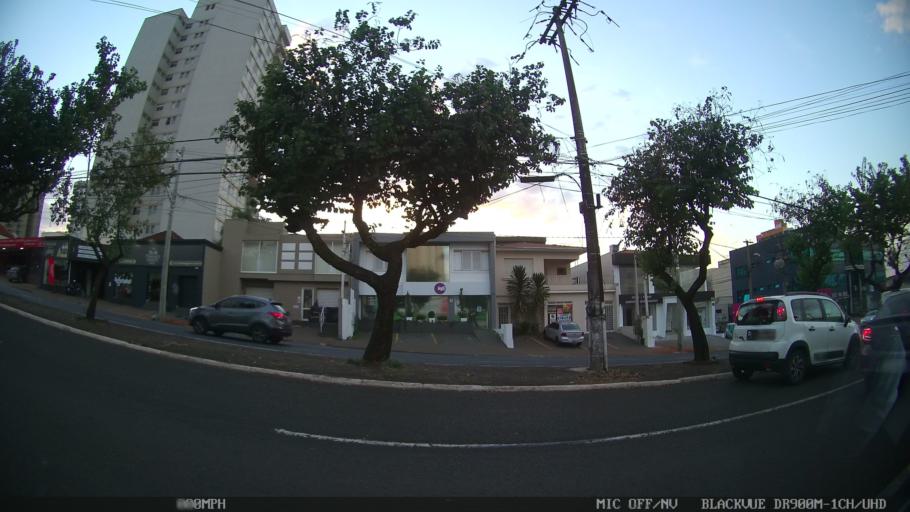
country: BR
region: Sao Paulo
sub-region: Ribeirao Preto
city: Ribeirao Preto
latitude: -21.1844
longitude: -47.8039
